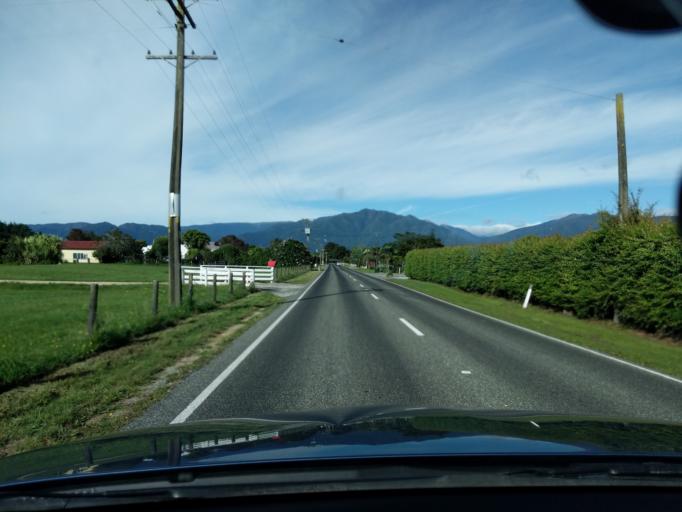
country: NZ
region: Tasman
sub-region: Tasman District
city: Takaka
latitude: -40.8550
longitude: 172.8252
